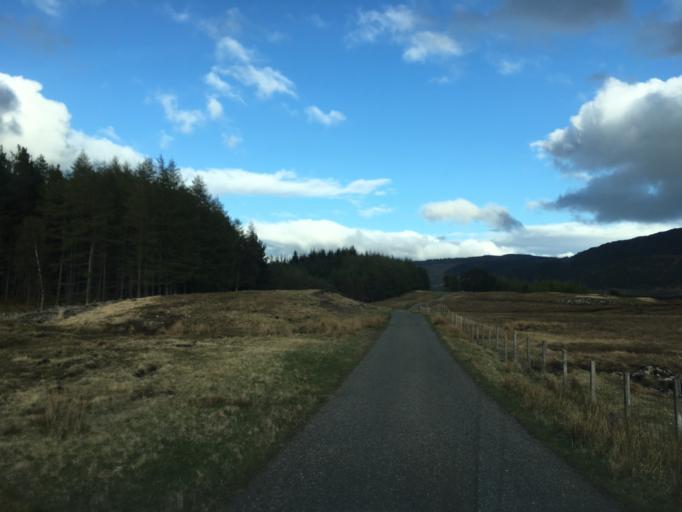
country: GB
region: Scotland
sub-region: Highland
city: Kingussie
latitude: 57.0097
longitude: -4.4119
